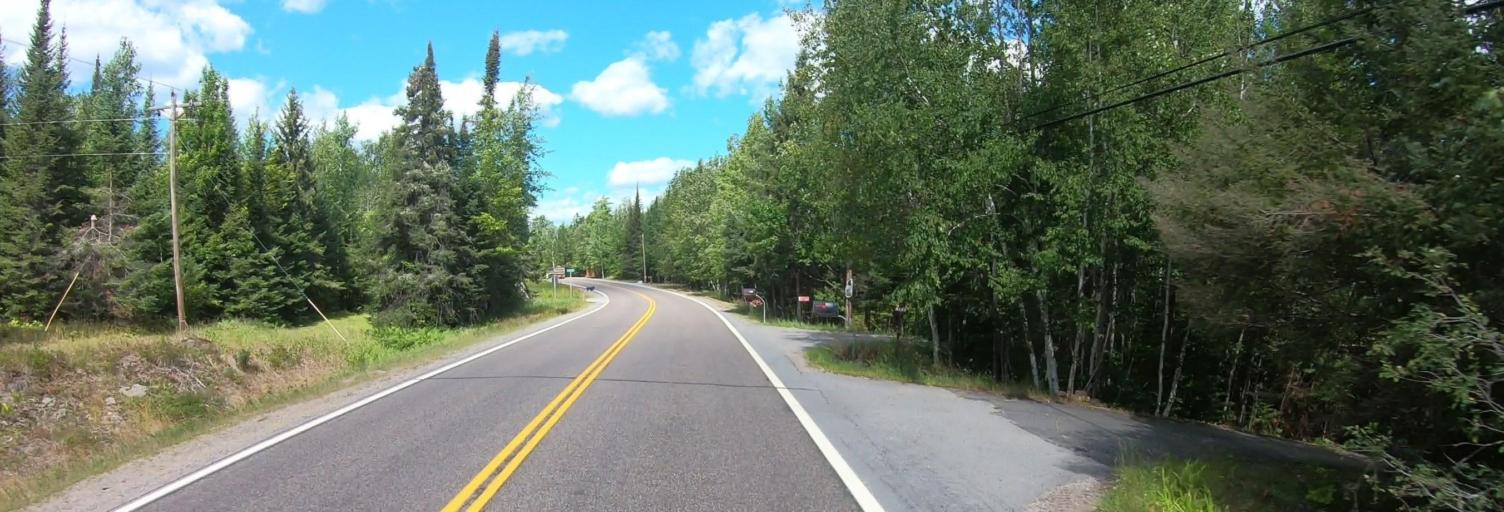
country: US
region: Minnesota
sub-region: Saint Louis County
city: Mountain Iron
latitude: 47.9257
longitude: -92.6619
